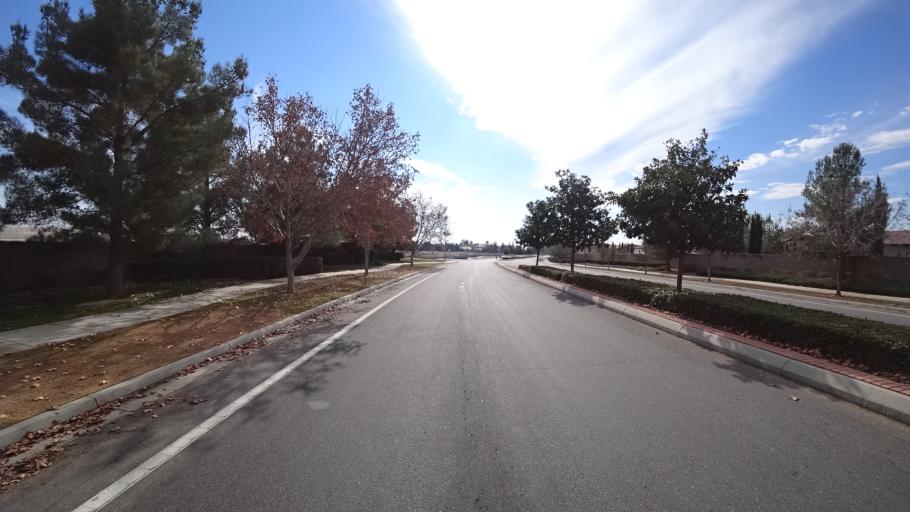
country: US
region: California
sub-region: Kern County
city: Oildale
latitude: 35.4069
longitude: -118.8866
